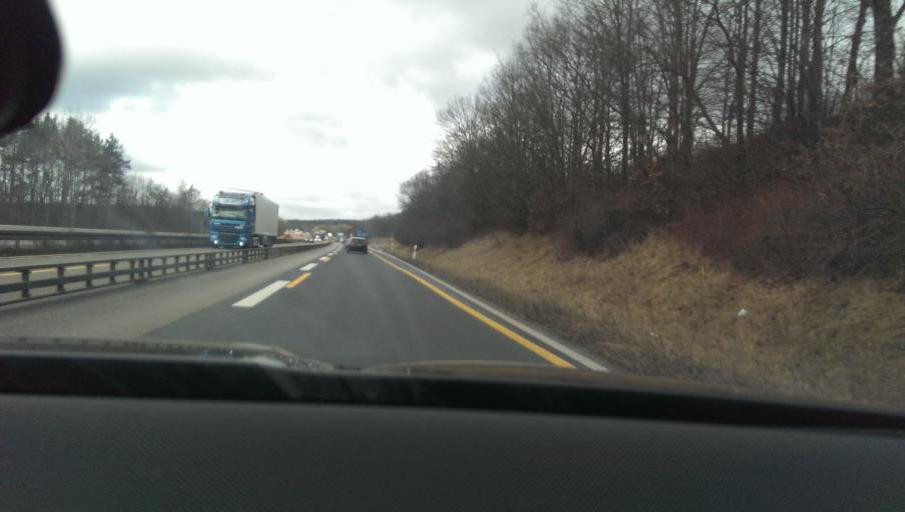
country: DE
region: Hesse
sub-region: Regierungsbezirk Kassel
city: Petersberg
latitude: 50.5796
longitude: 9.7125
